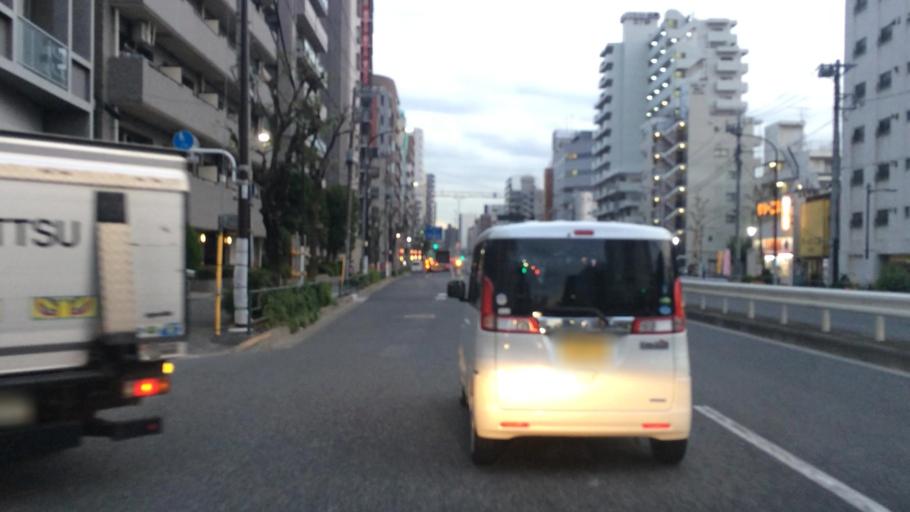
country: JP
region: Tokyo
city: Tokyo
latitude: 35.6348
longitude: 139.7070
